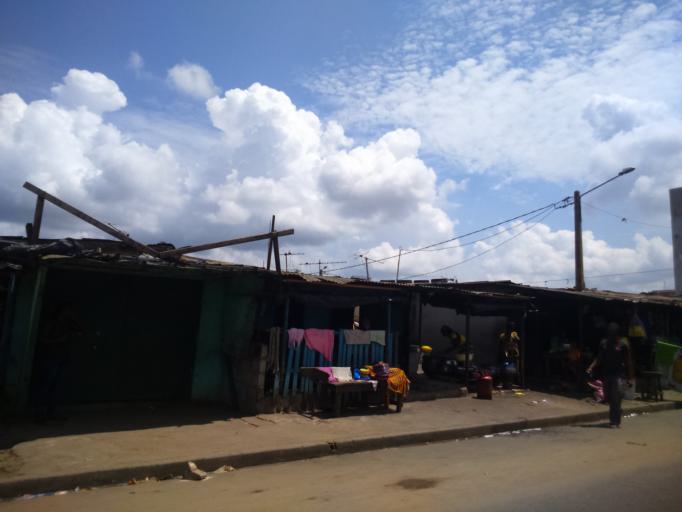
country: CI
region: Lagunes
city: Abidjan
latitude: 5.3506
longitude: -4.0875
